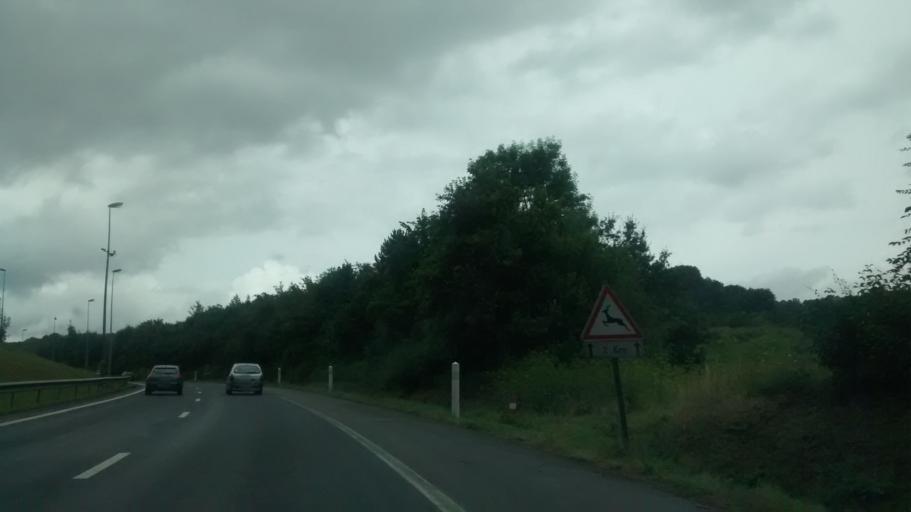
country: FR
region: Haute-Normandie
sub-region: Departement de la Seine-Maritime
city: Darnetal
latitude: 49.4509
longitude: 1.1455
